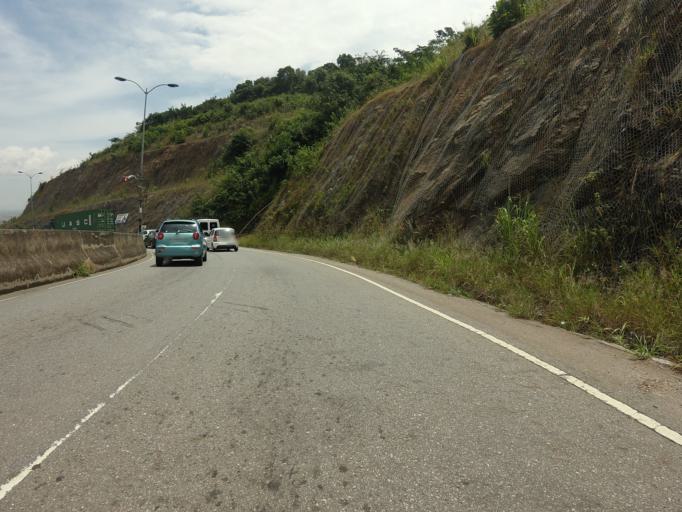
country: GH
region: Eastern
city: Aburi
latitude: 5.7946
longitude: -0.1867
